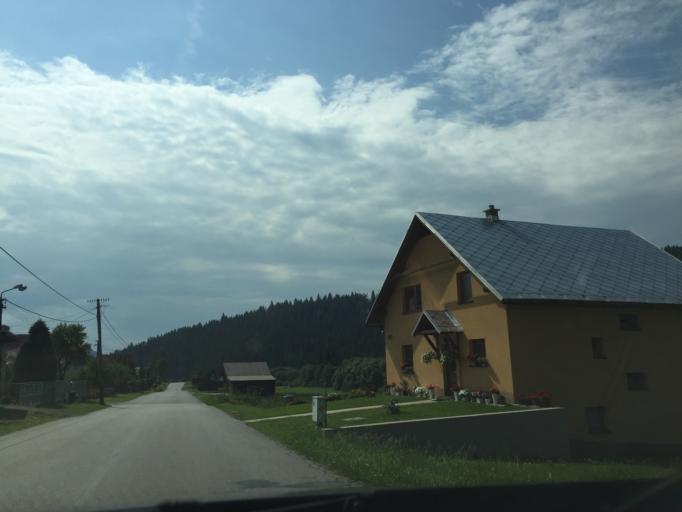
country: PL
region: Silesian Voivodeship
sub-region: Powiat zywiecki
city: Korbielow
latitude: 49.4361
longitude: 19.3162
